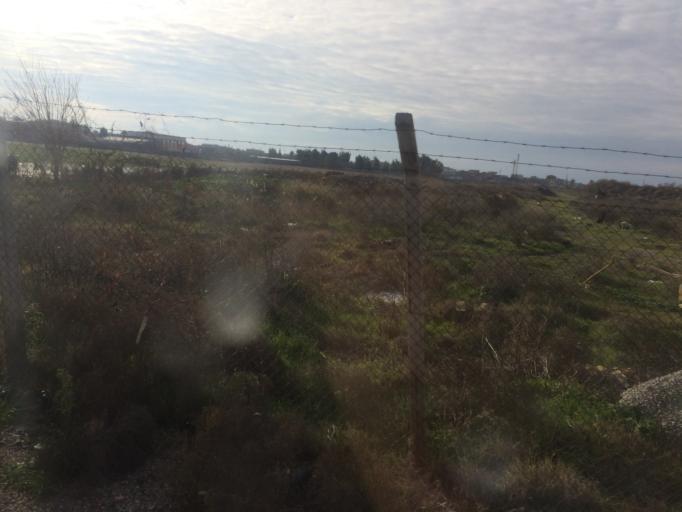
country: TR
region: Izmir
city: Karsiyaka
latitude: 38.4966
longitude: 26.9601
